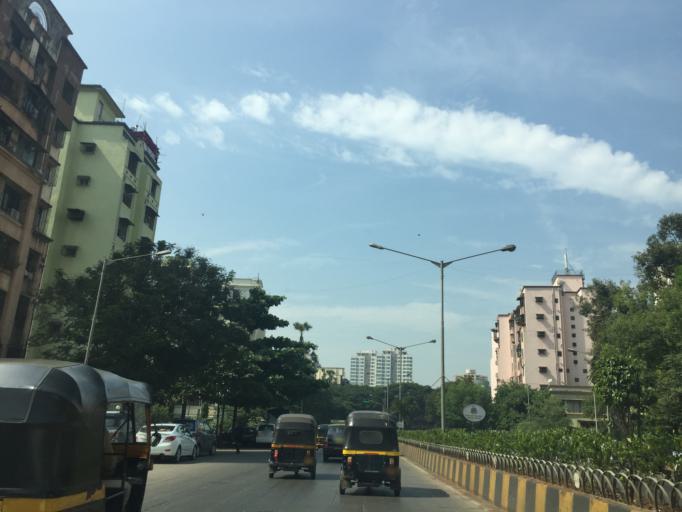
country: IN
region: Maharashtra
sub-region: Mumbai Suburban
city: Borivli
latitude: 19.2197
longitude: 72.8425
